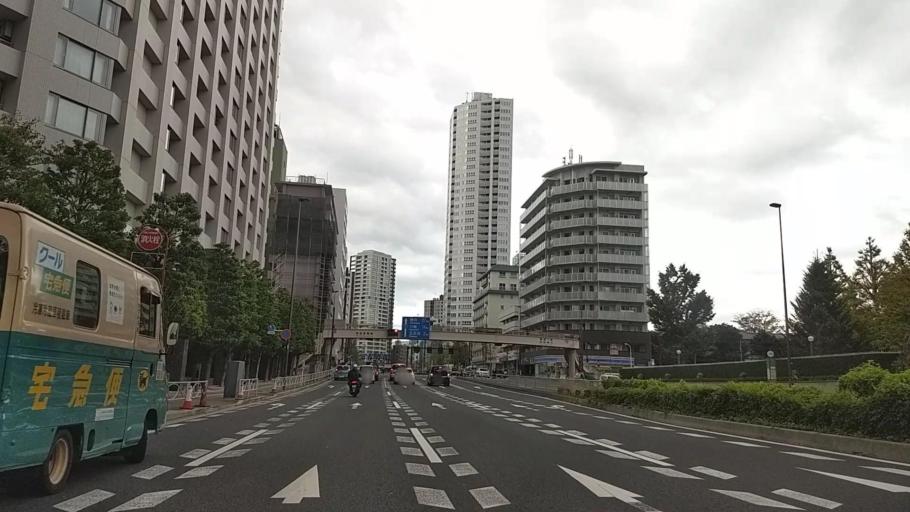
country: JP
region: Tokyo
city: Tokyo
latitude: 35.6368
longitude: 139.7316
